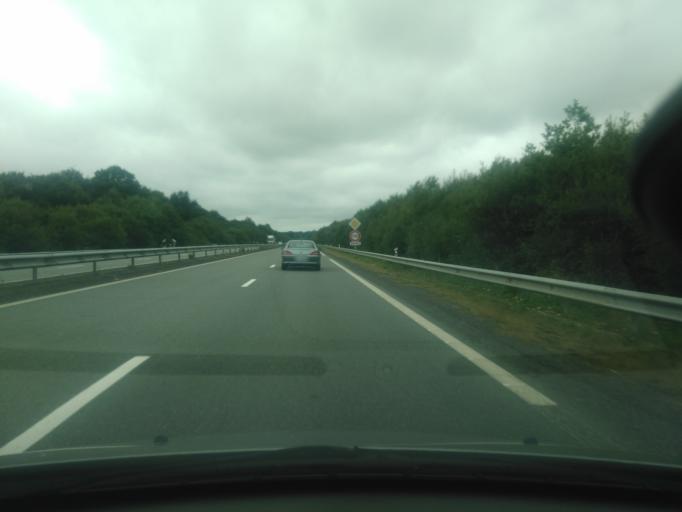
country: FR
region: Brittany
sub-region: Departement des Cotes-d'Armor
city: Plelan-le-Petit
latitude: 48.4256
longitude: -2.1946
